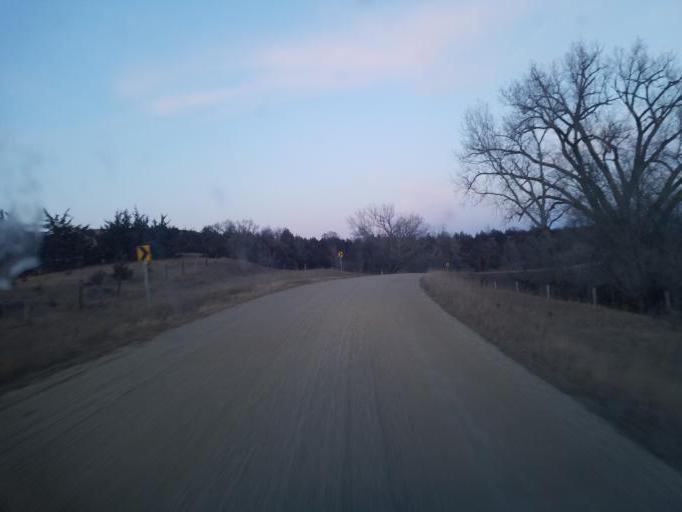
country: US
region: Nebraska
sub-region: Knox County
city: Center
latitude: 42.6146
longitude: -97.8493
